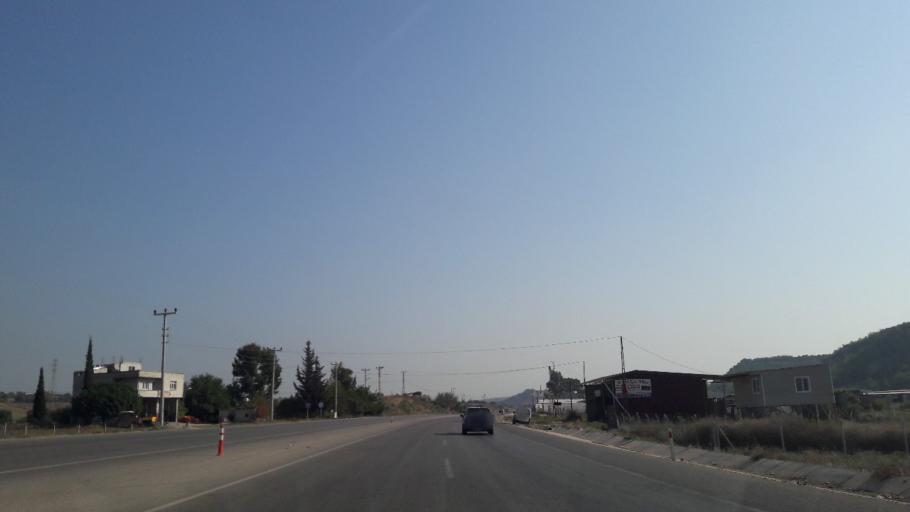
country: TR
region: Adana
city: Yuregir
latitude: 37.0649
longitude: 35.4477
